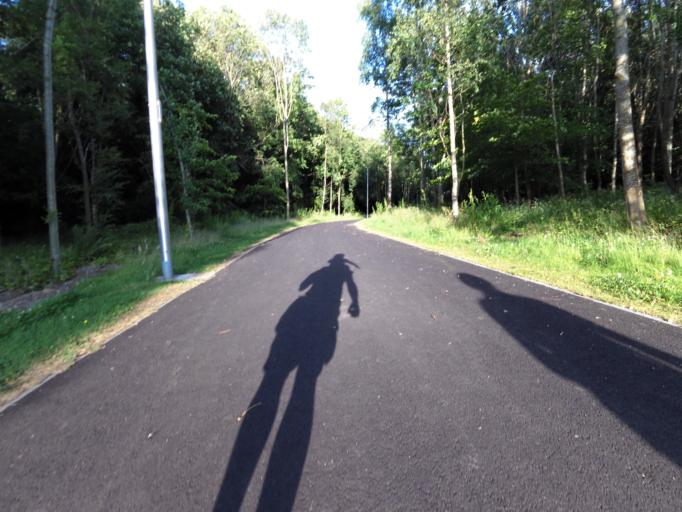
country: GB
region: Scotland
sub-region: West Lothian
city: Seafield
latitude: 55.9270
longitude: -3.1379
